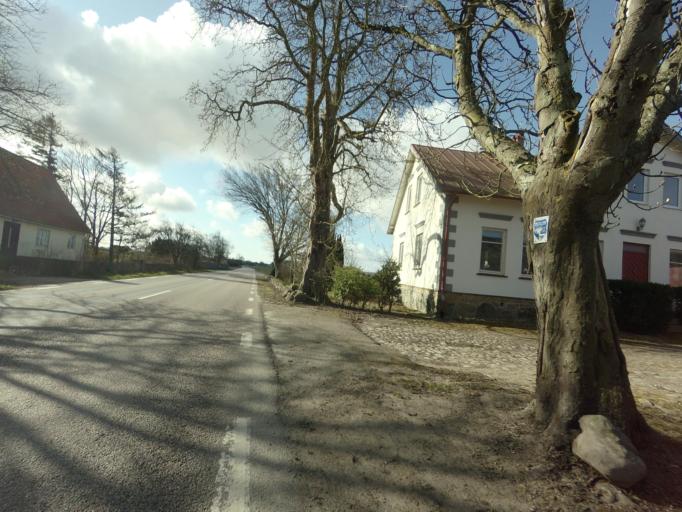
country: SE
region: Skane
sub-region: Helsingborg
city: Odakra
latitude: 56.1592
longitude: 12.6785
